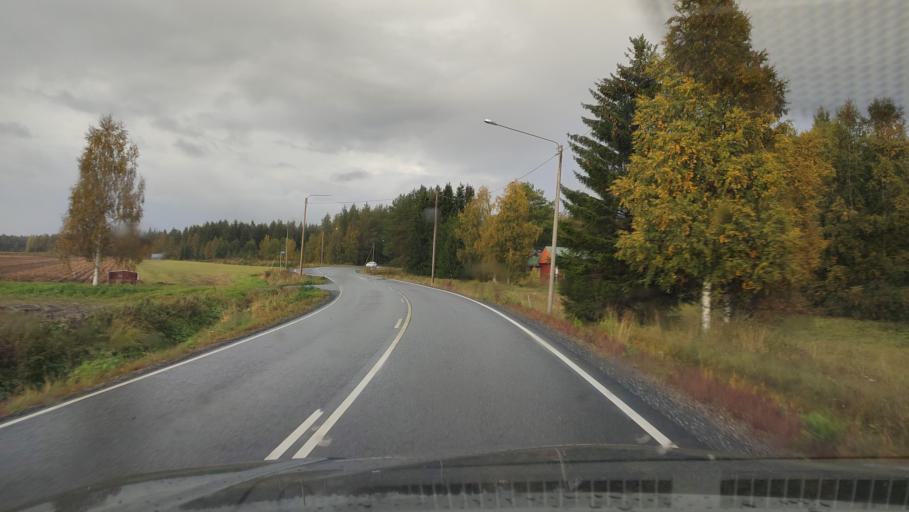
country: FI
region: Southern Ostrobothnia
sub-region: Suupohja
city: Karijoki
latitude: 62.2699
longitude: 21.5602
